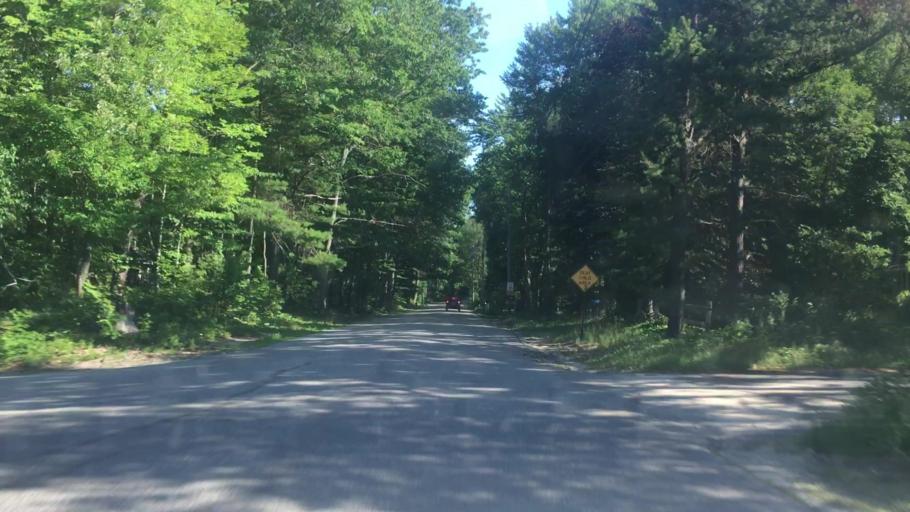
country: US
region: Maine
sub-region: Cumberland County
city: Gorham
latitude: 43.7222
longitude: -70.5155
